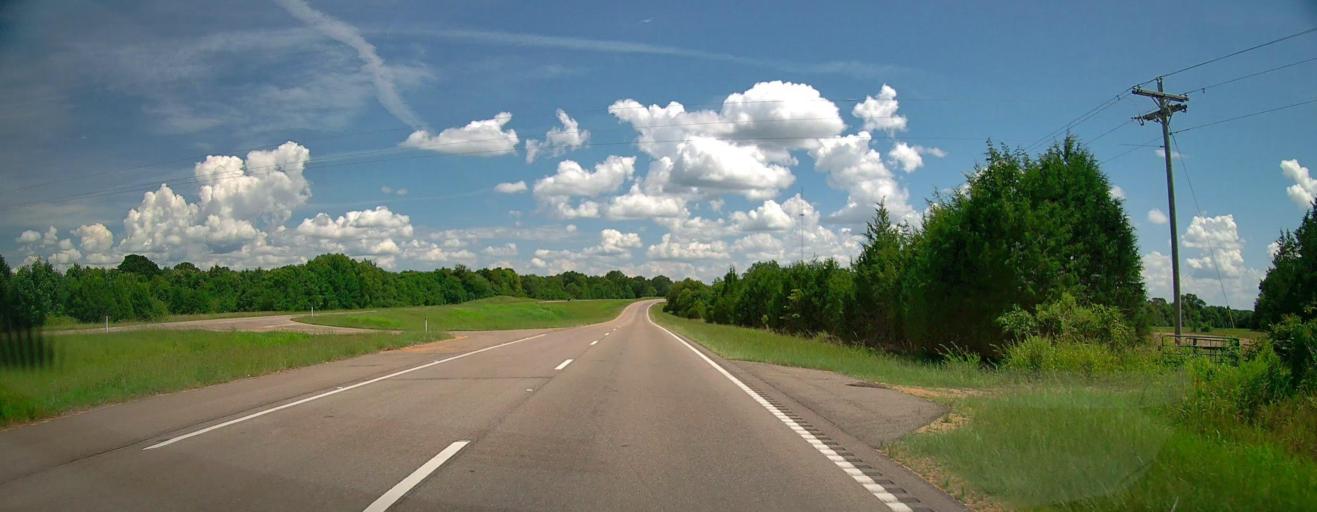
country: US
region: Mississippi
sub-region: Monroe County
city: Amory
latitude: 33.9566
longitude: -88.6080
